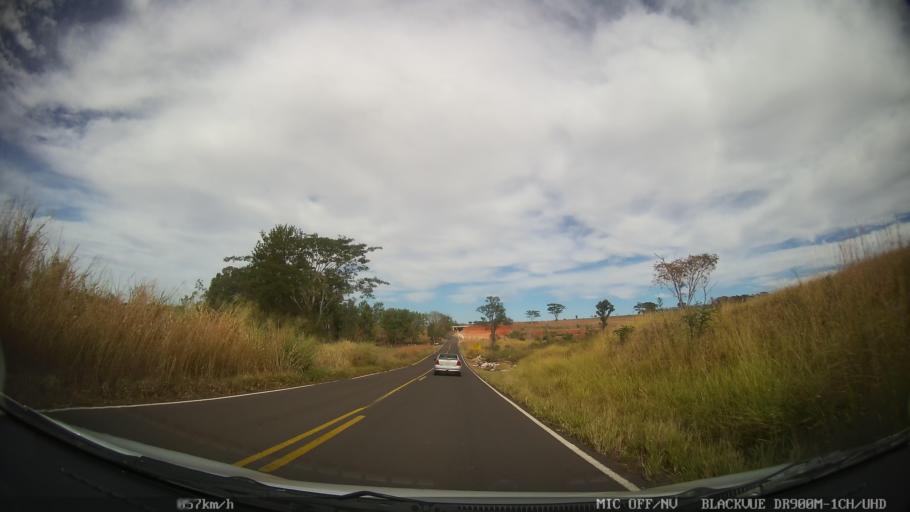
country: BR
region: Sao Paulo
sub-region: Catanduva
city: Catanduva
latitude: -21.1753
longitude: -48.9628
